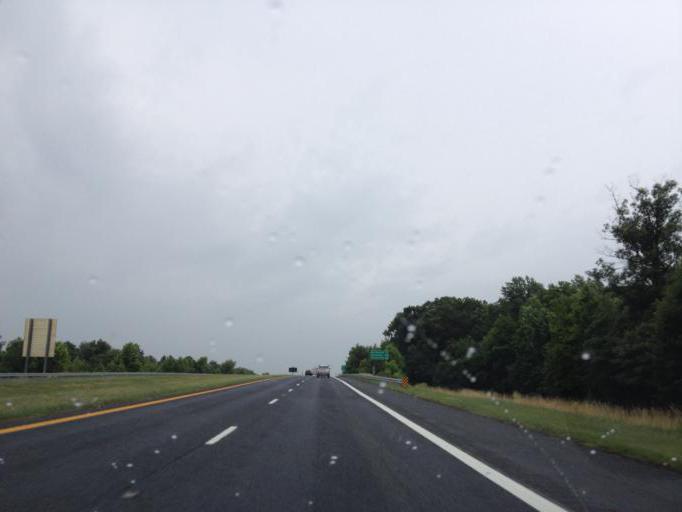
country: US
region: Maryland
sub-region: Caroline County
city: Denton
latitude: 38.8866
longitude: -75.8143
